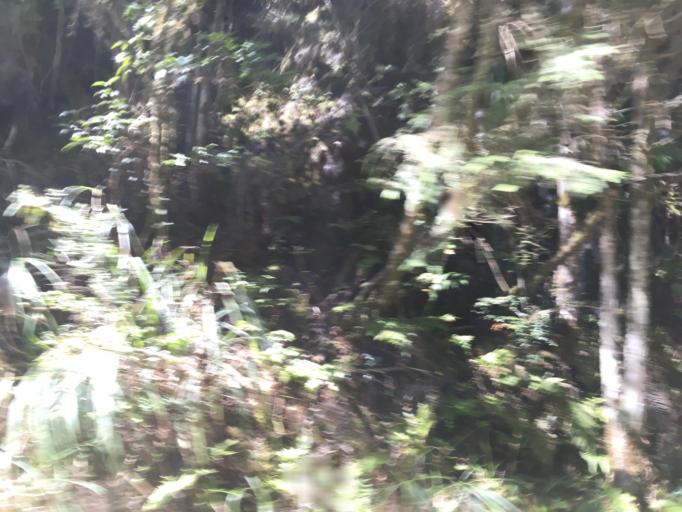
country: TW
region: Taiwan
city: Daxi
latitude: 24.5882
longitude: 121.4113
